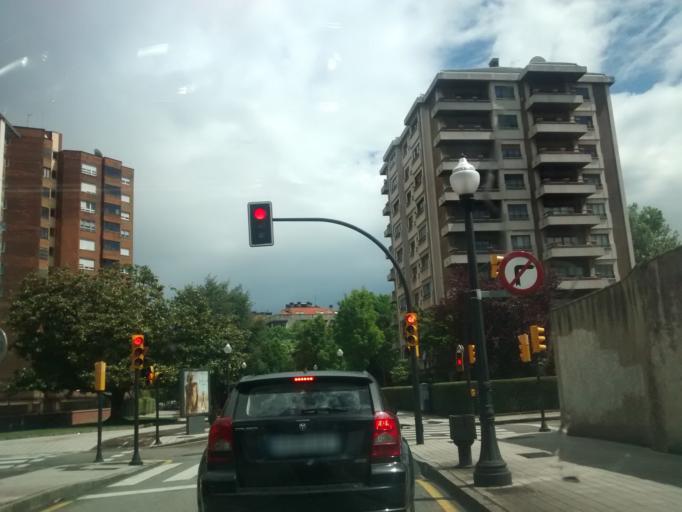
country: ES
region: Asturias
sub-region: Province of Asturias
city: Gijon
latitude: 43.5341
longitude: -5.6429
